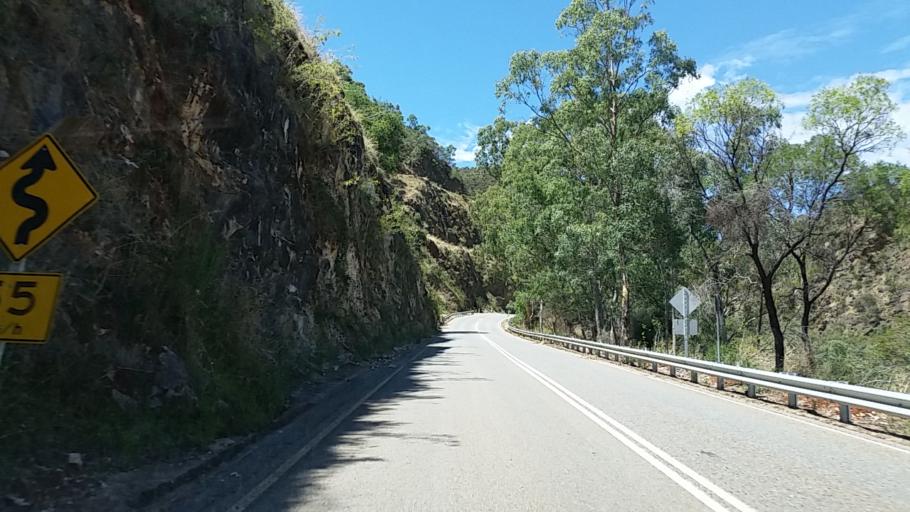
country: AU
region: South Australia
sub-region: Campbelltown
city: Athelstone
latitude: -34.8643
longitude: 138.7599
